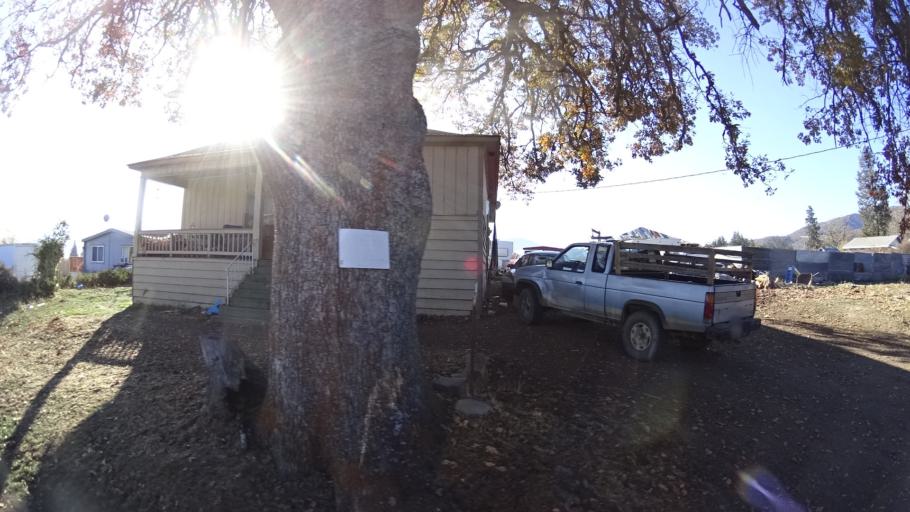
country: US
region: California
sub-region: Siskiyou County
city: Montague
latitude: 41.9090
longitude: -122.5620
